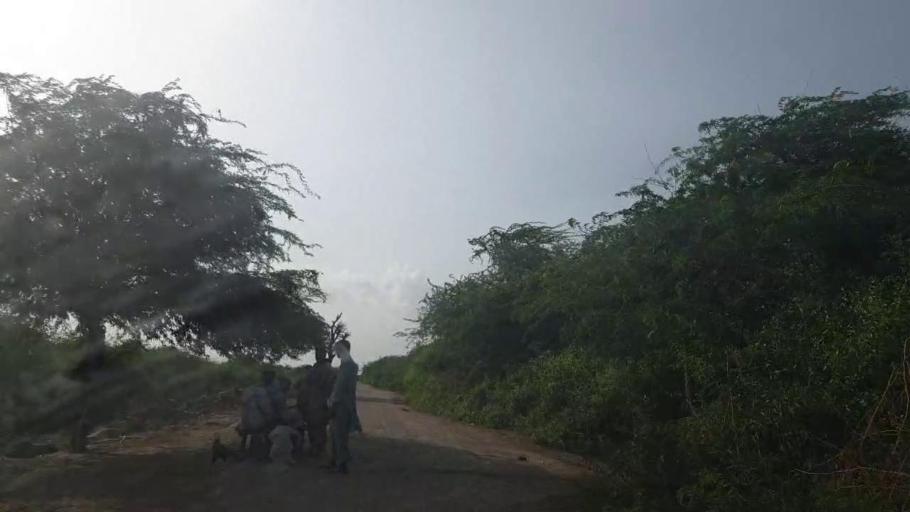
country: PK
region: Sindh
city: Tando Bago
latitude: 24.7572
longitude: 69.0841
